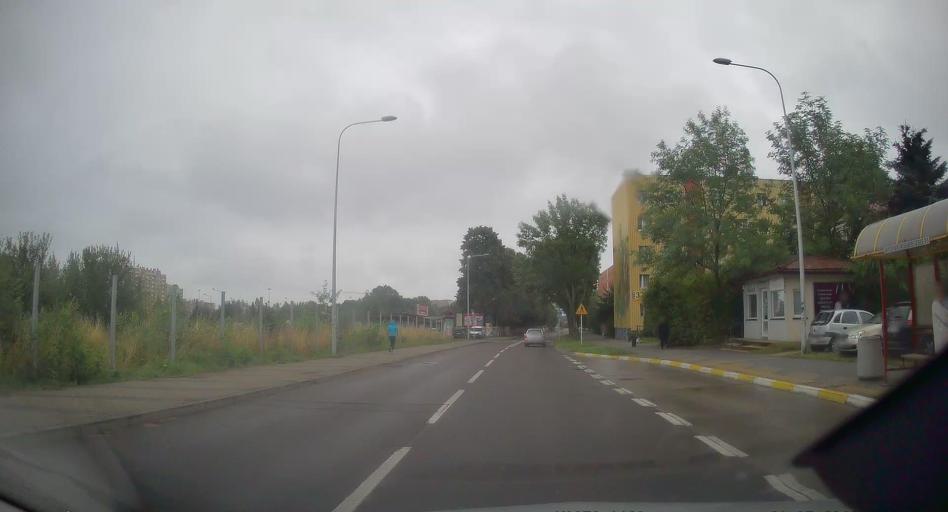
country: PL
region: Subcarpathian Voivodeship
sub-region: Rzeszow
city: Rzeszow
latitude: 50.0398
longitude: 21.9810
